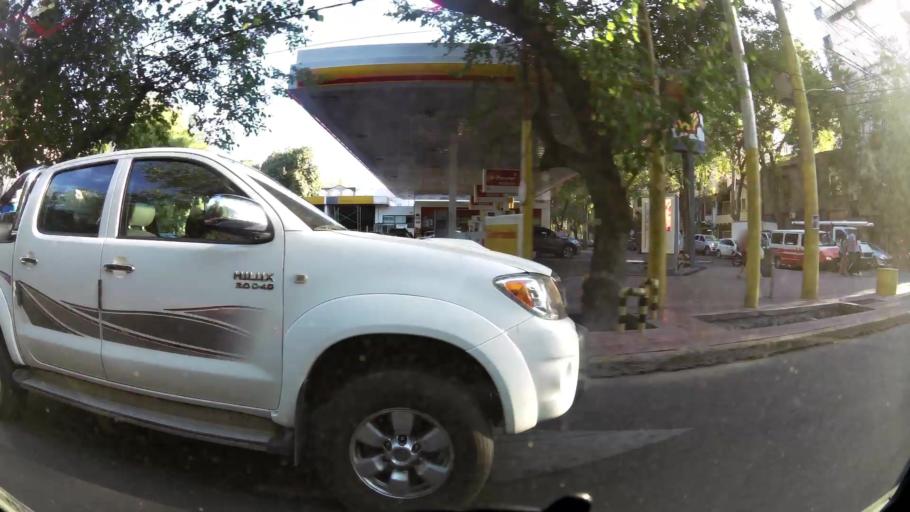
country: AR
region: Mendoza
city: Mendoza
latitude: -32.8946
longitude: -68.8429
